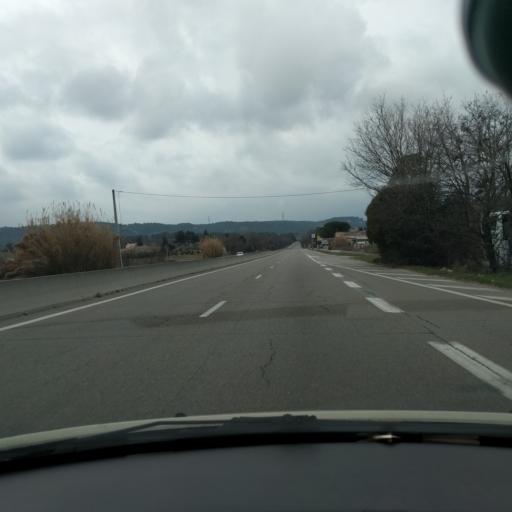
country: FR
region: Provence-Alpes-Cote d'Azur
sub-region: Departement des Bouches-du-Rhone
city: Simiane-Collongue
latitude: 43.4429
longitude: 5.4363
